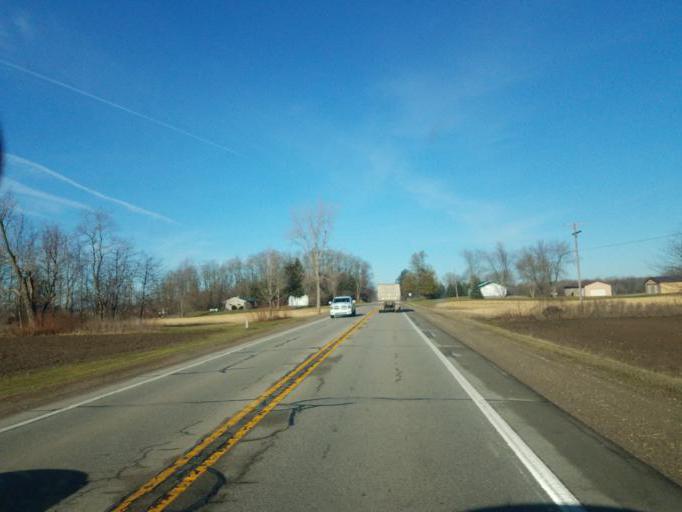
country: US
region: Michigan
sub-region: Gratiot County
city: Alma
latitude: 43.4083
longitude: -84.7187
